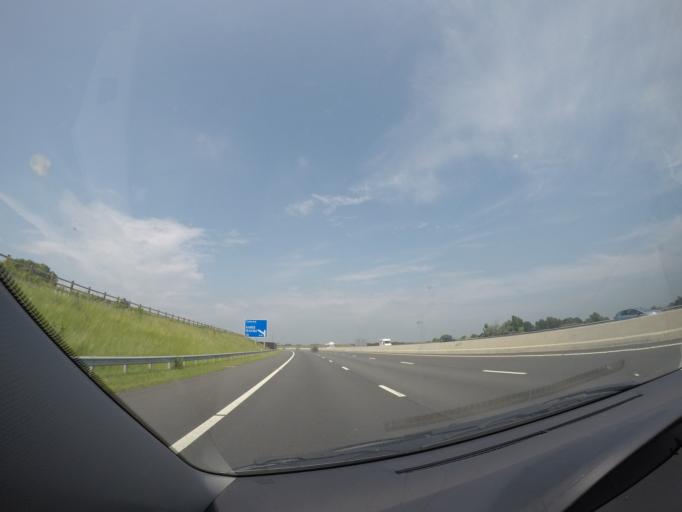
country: GB
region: England
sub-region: North Yorkshire
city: Catterick
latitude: 54.3699
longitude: -1.6363
